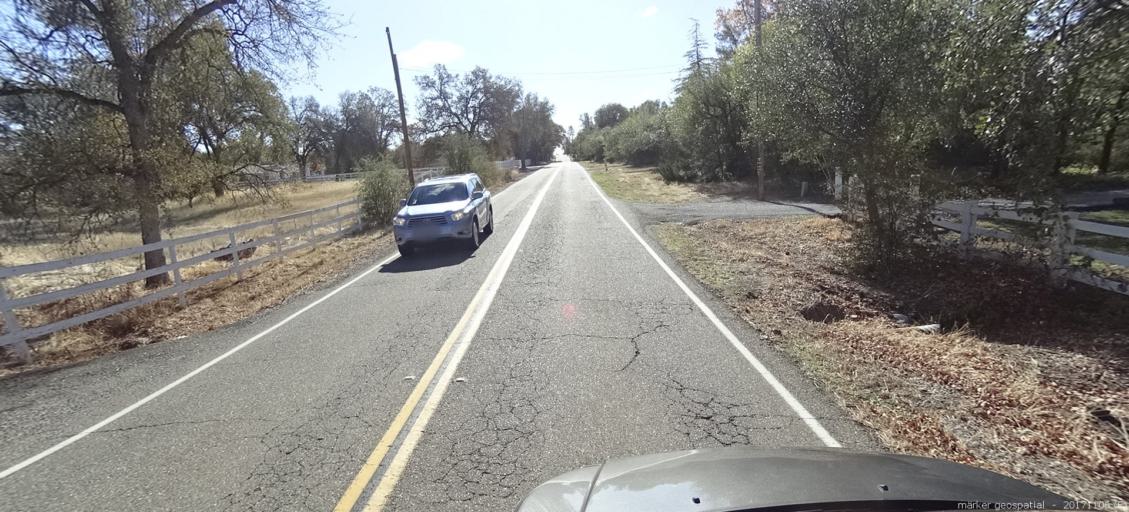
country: US
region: California
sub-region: Shasta County
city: Palo Cedro
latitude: 40.5709
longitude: -122.2199
